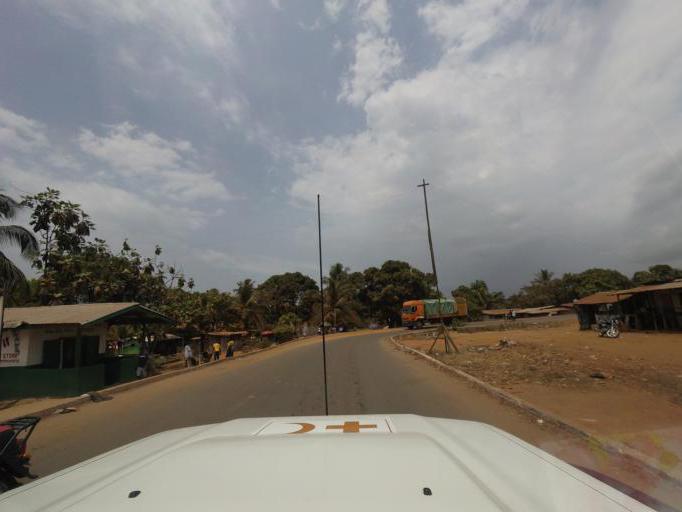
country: LR
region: Montserrado
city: Monrovia
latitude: 6.3085
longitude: -10.6984
